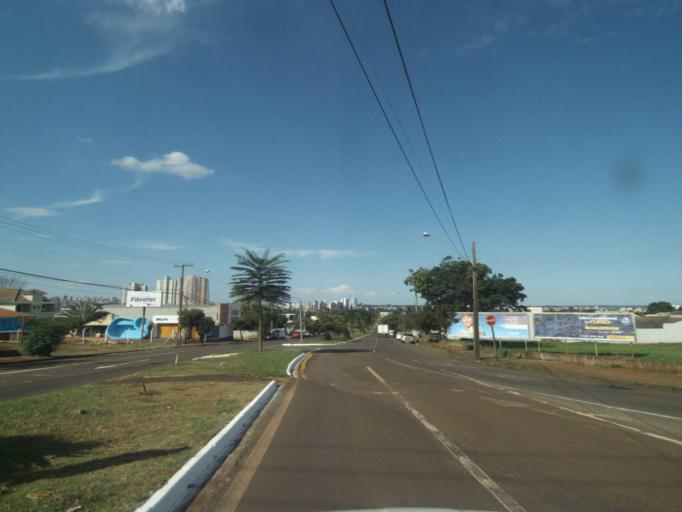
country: BR
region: Parana
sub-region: Londrina
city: Londrina
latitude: -23.3494
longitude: -51.1671
